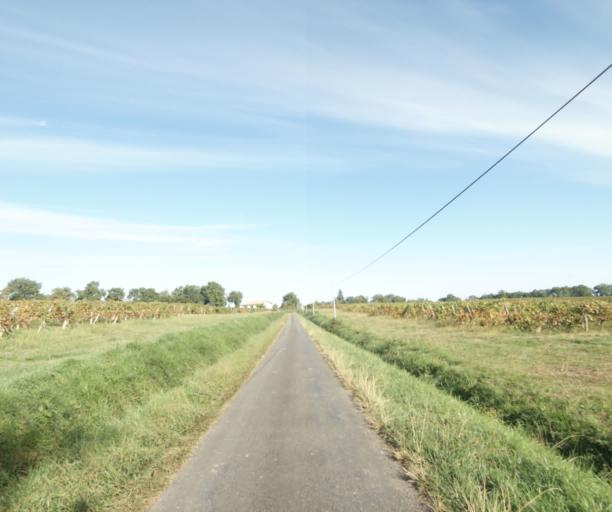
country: FR
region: Midi-Pyrenees
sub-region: Departement du Gers
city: Eauze
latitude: 43.8880
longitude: 0.1332
